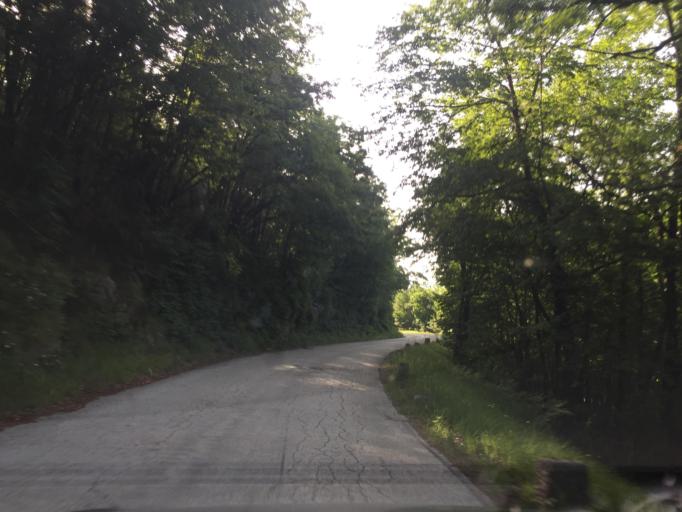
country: HR
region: Istarska
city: Buzet
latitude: 45.4729
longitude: 14.0954
